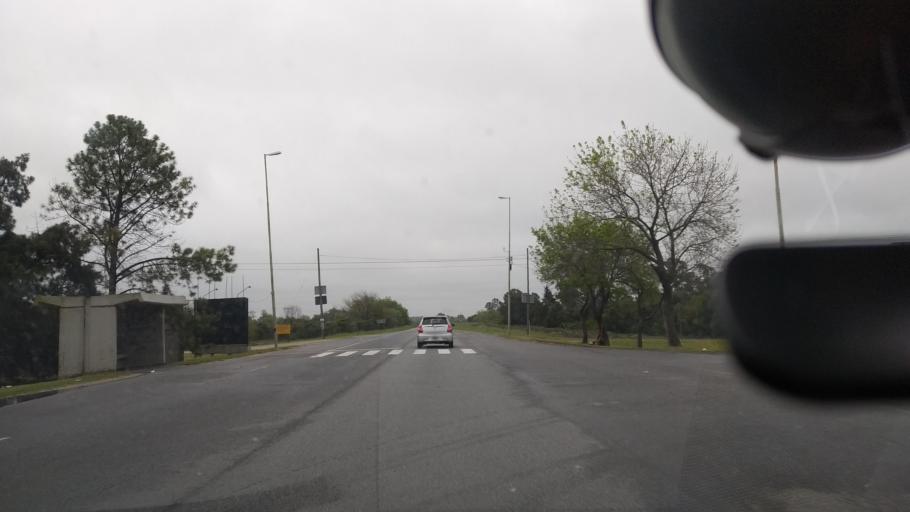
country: AR
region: Buenos Aires
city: Veronica
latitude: -35.4001
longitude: -57.3539
